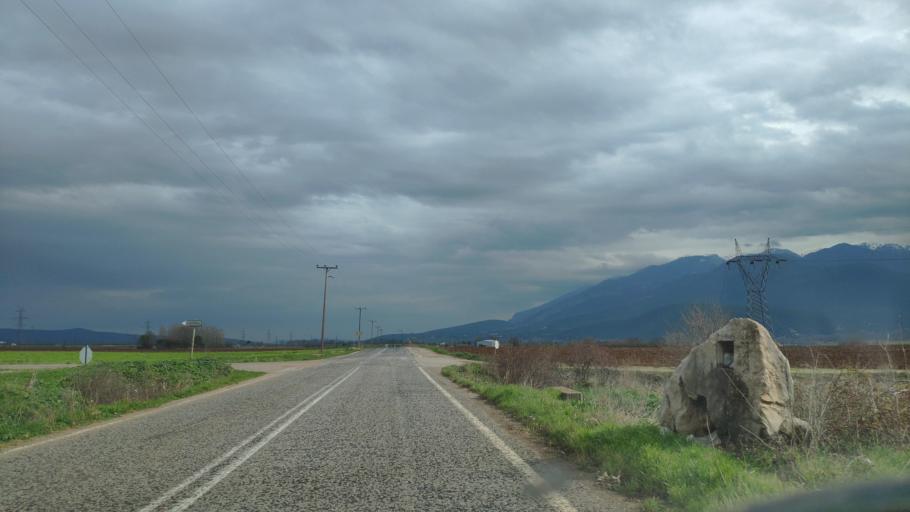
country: GR
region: Central Greece
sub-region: Nomos Fthiotidos
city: Amfikleia
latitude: 38.6961
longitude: 22.5227
